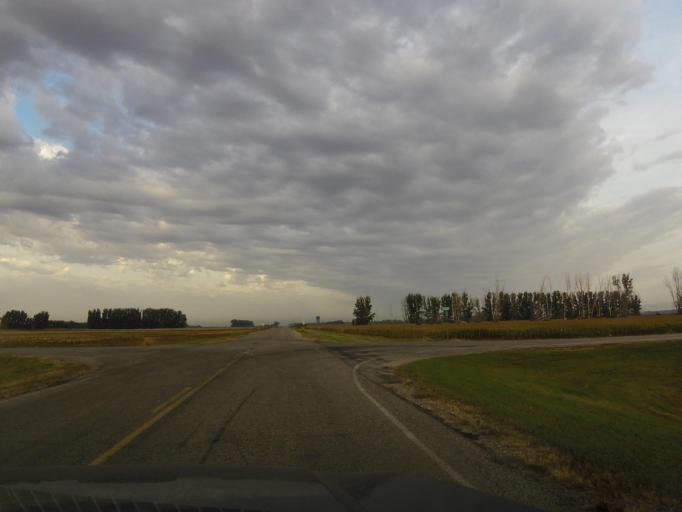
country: US
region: North Dakota
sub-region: Pembina County
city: Cavalier
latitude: 48.6881
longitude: -97.7314
